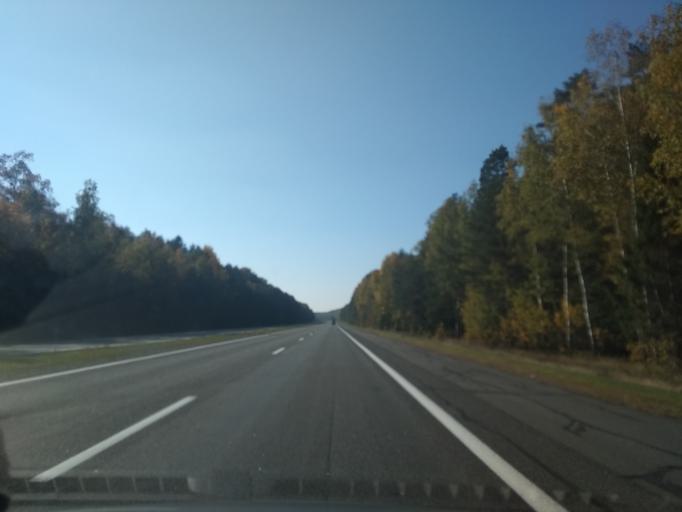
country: BY
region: Brest
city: Ivatsevichy
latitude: 52.8377
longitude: 25.6140
